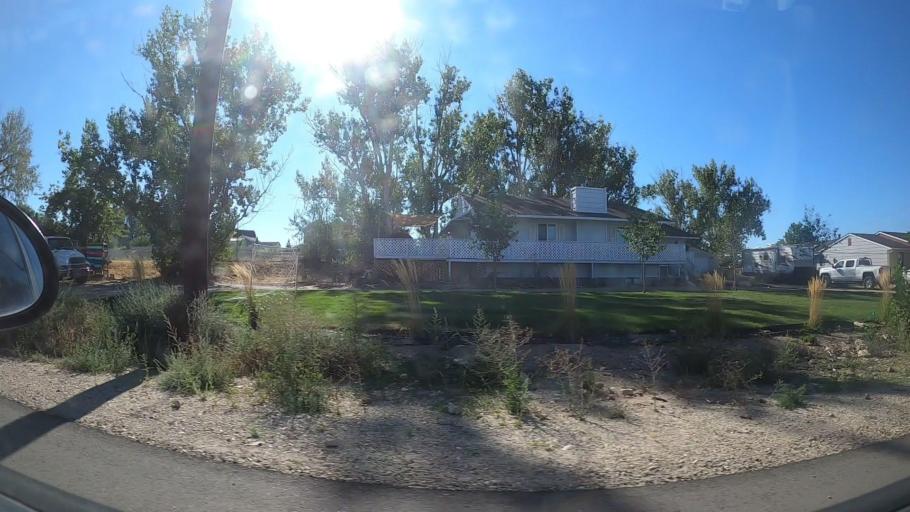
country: US
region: Idaho
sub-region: Canyon County
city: Nampa
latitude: 43.5611
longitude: -116.6129
